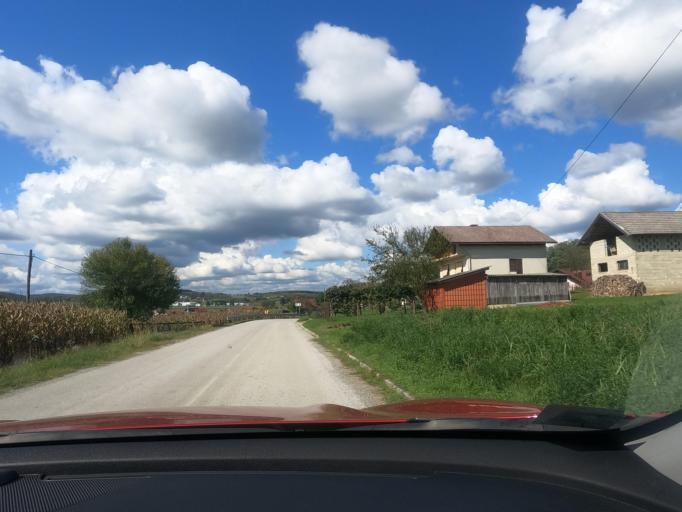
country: BA
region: Federation of Bosnia and Herzegovina
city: Velika Kladusa
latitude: 45.2013
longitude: 15.7977
